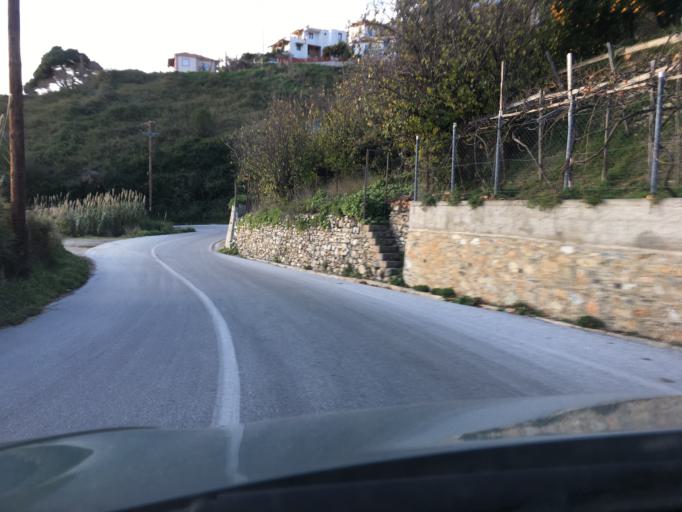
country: GR
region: Thessaly
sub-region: Nomos Magnisias
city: Skopelos
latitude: 39.1736
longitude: 23.6167
